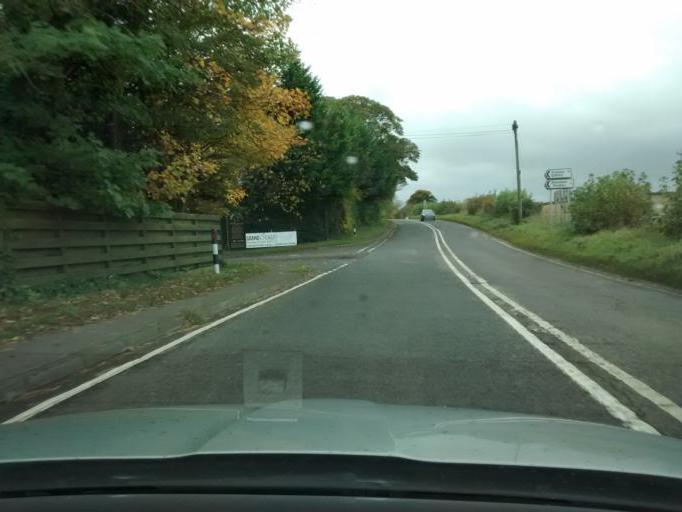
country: GB
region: Scotland
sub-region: Perth and Kinross
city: Auchterarder
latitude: 56.3052
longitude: -3.6771
